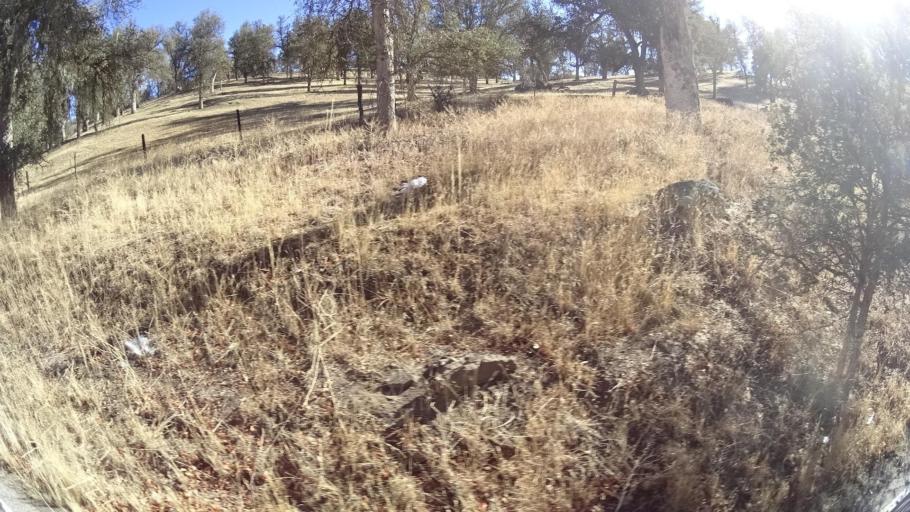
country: US
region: California
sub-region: Kern County
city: Alta Sierra
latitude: 35.7448
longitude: -118.7177
